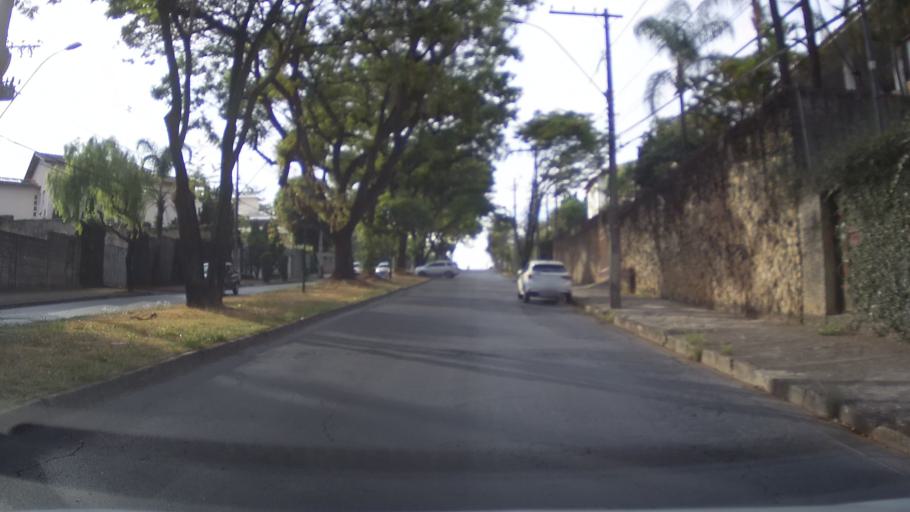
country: BR
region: Minas Gerais
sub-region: Belo Horizonte
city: Belo Horizonte
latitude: -19.8643
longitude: -43.9902
